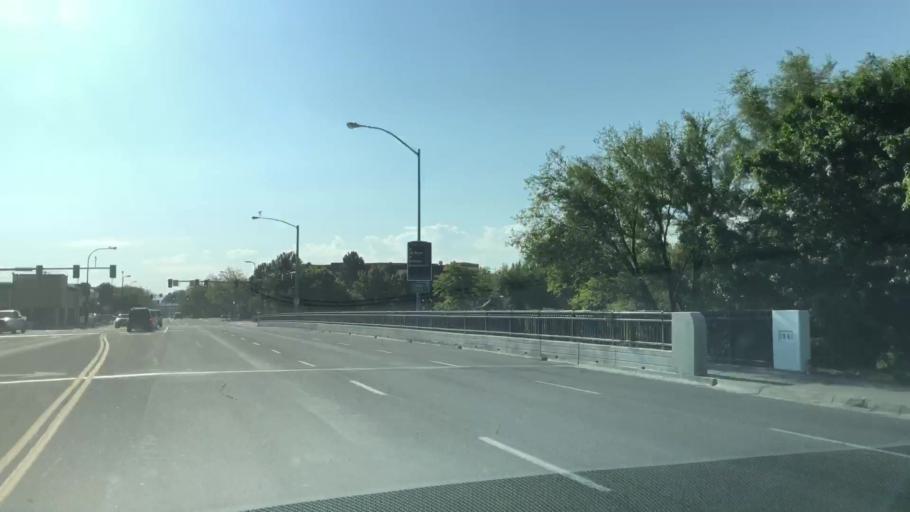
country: US
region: Idaho
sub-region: Bonneville County
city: Idaho Falls
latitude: 43.4932
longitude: -112.0452
